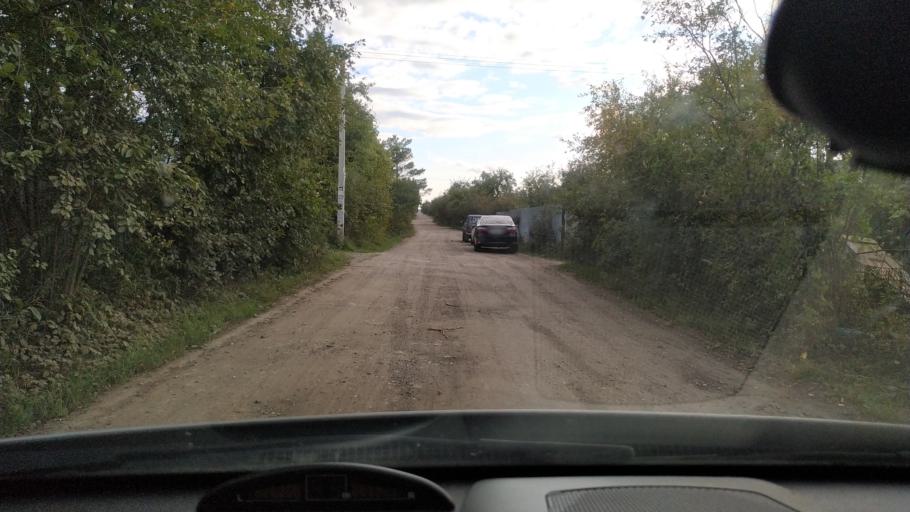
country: RU
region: Rjazan
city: Polyany
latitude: 54.5588
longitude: 39.8775
